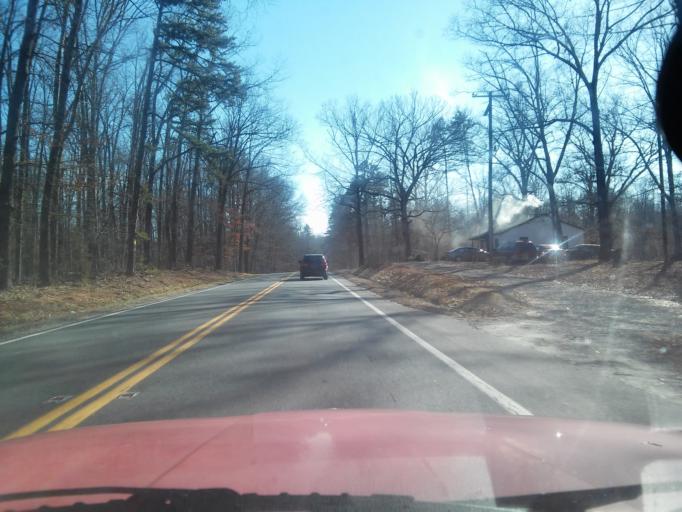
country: US
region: Virginia
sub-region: Orange County
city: Gordonsville
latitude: 38.0048
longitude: -78.1919
